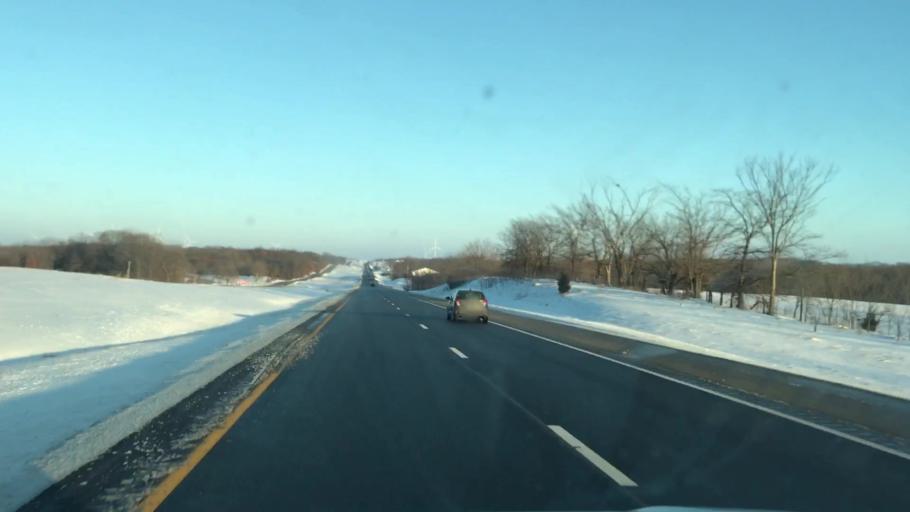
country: US
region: Missouri
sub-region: DeKalb County
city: Maysville
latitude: 39.7620
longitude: -94.4907
